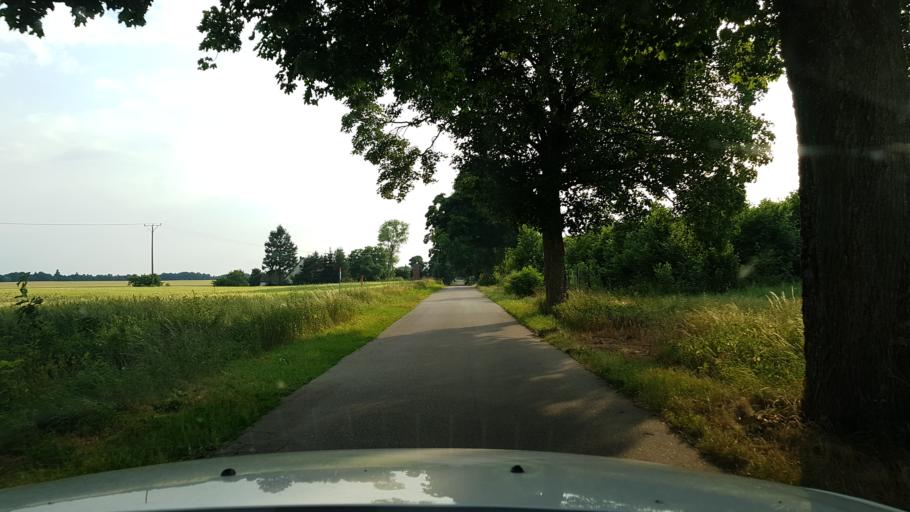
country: PL
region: West Pomeranian Voivodeship
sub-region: Powiat swidwinski
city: Rabino
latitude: 53.8132
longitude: 15.8771
